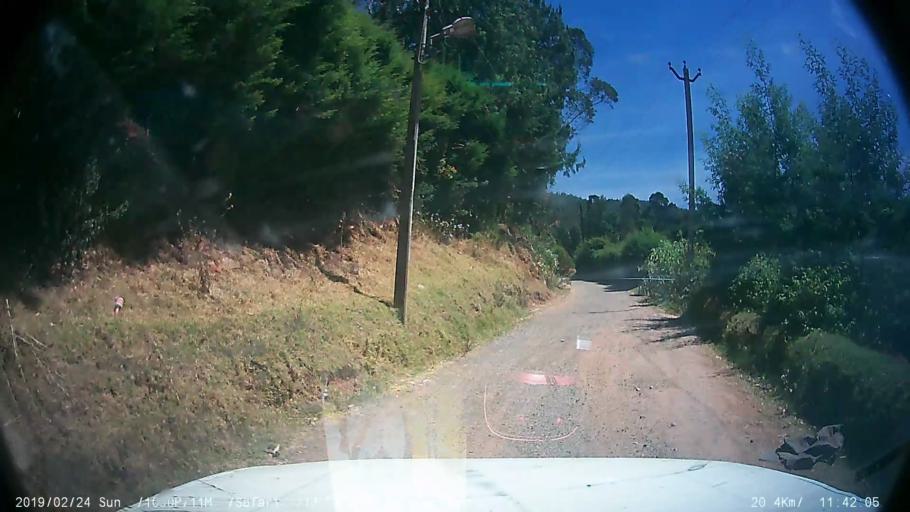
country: IN
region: Tamil Nadu
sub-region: Nilgiri
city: Ooty
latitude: 11.4193
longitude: 76.7045
